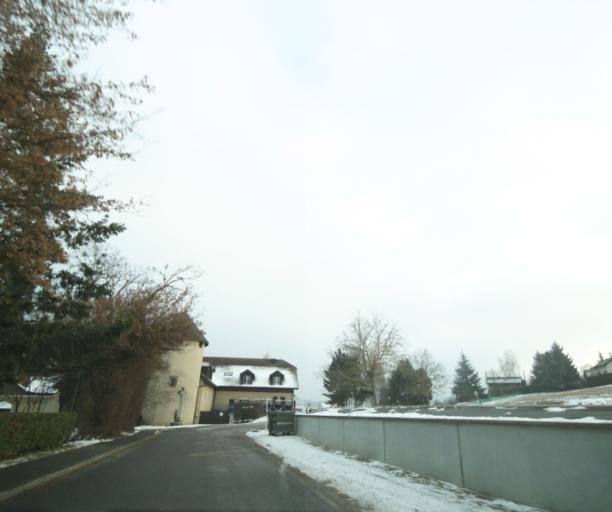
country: FR
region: Rhone-Alpes
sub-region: Departement de la Haute-Savoie
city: Reignier-Esery
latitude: 46.1431
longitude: 6.2384
